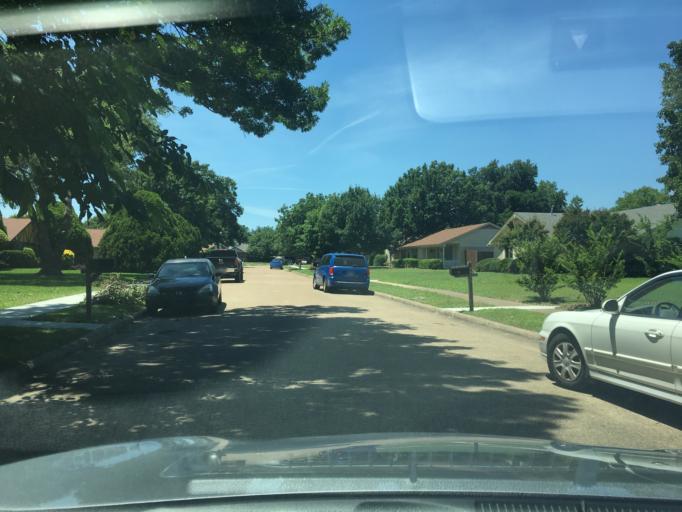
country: US
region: Texas
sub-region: Dallas County
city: Richardson
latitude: 32.9437
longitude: -96.6888
